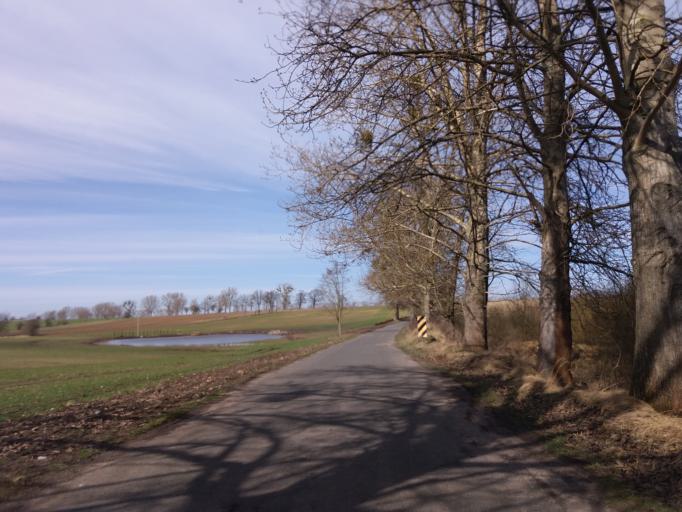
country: PL
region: West Pomeranian Voivodeship
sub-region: Powiat choszczenski
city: Choszczno
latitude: 53.1199
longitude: 15.3983
